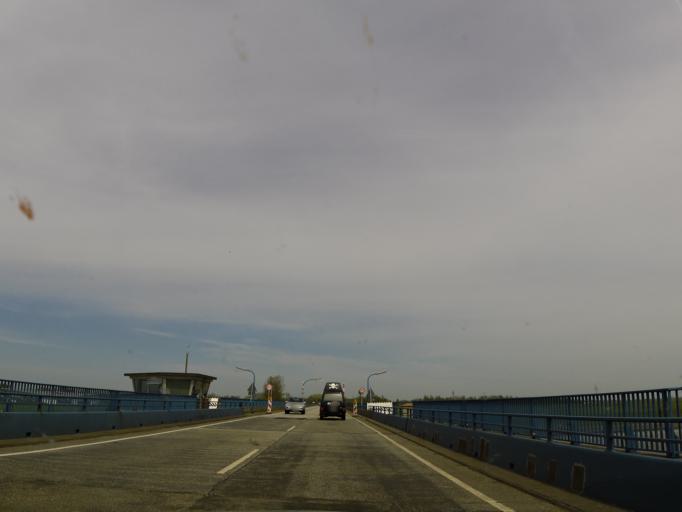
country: DE
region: Schleswig-Holstein
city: Tonning
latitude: 54.3145
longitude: 8.9565
